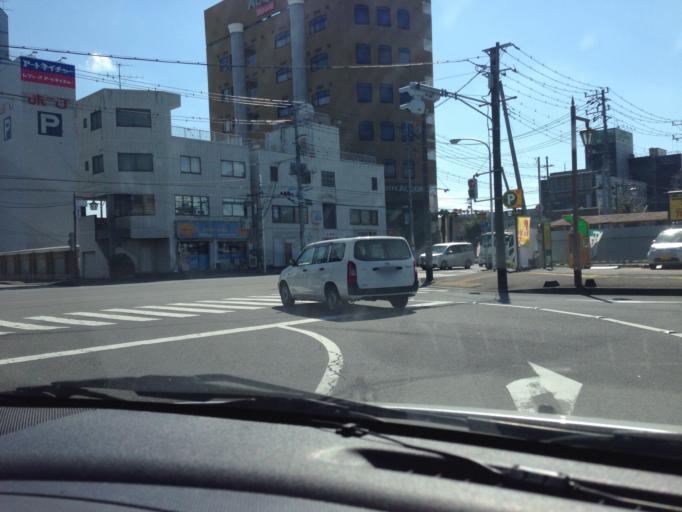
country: JP
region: Ibaraki
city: Ami
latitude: 36.0768
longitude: 140.2070
